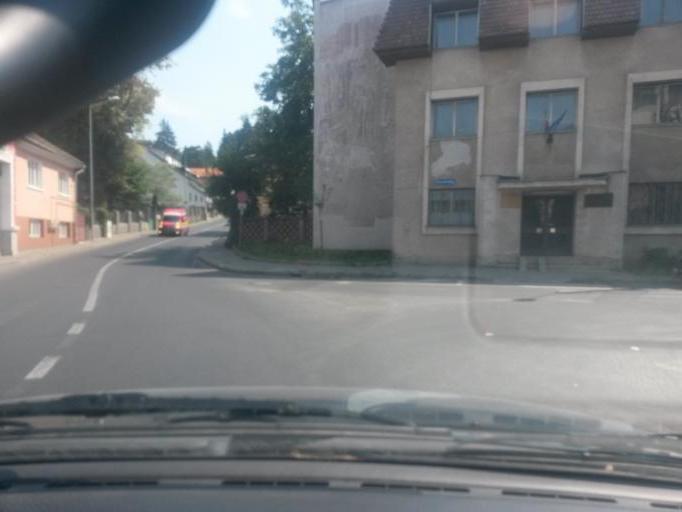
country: RO
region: Mures
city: Targu-Mures
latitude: 46.5456
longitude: 24.5692
